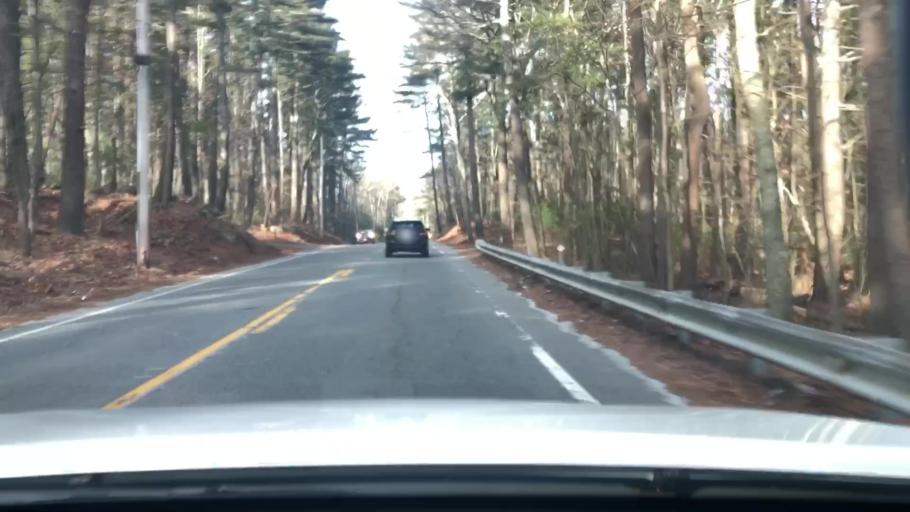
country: US
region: Massachusetts
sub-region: Worcester County
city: Grafton
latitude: 42.1961
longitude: -71.6563
